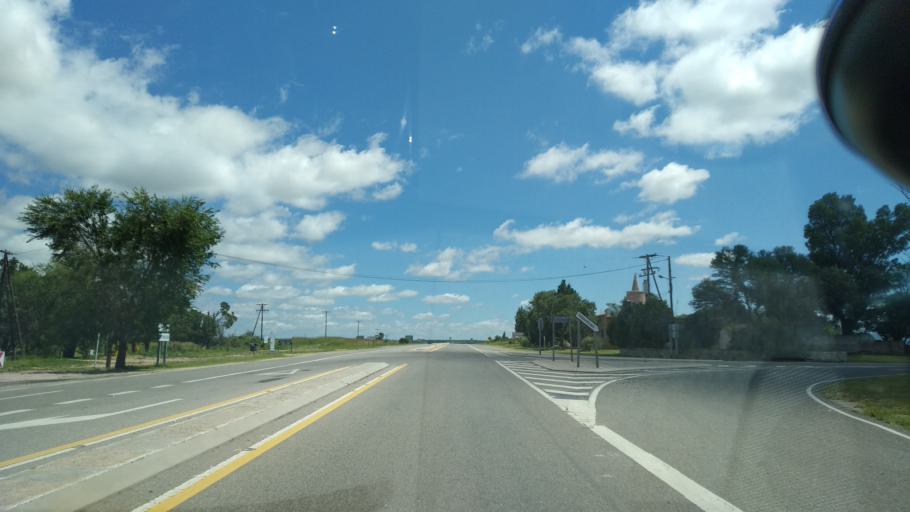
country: AR
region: Cordoba
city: Villa Cura Brochero
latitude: -31.6557
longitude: -65.0988
